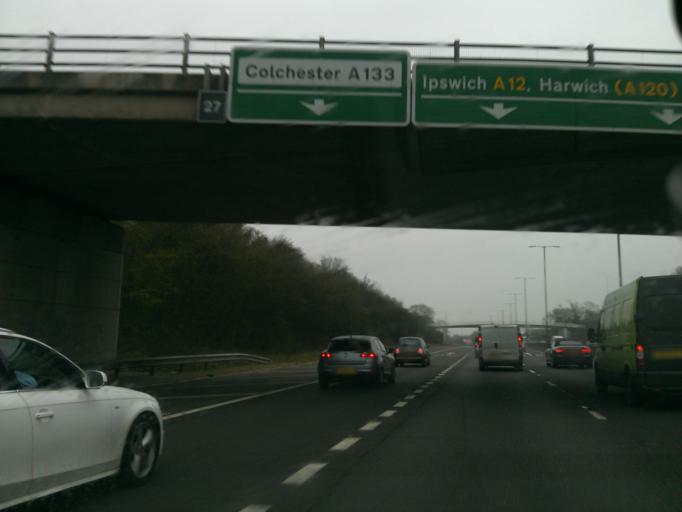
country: GB
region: England
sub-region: Essex
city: Eight Ash Green
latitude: 51.8914
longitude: 0.8421
